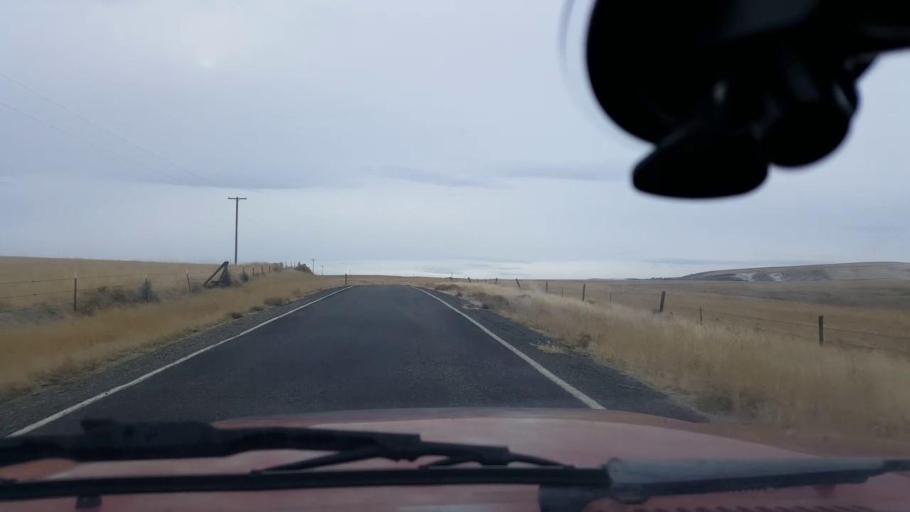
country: US
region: Washington
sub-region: Asotin County
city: Clarkston Heights-Vineland
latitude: 46.3296
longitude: -117.3216
